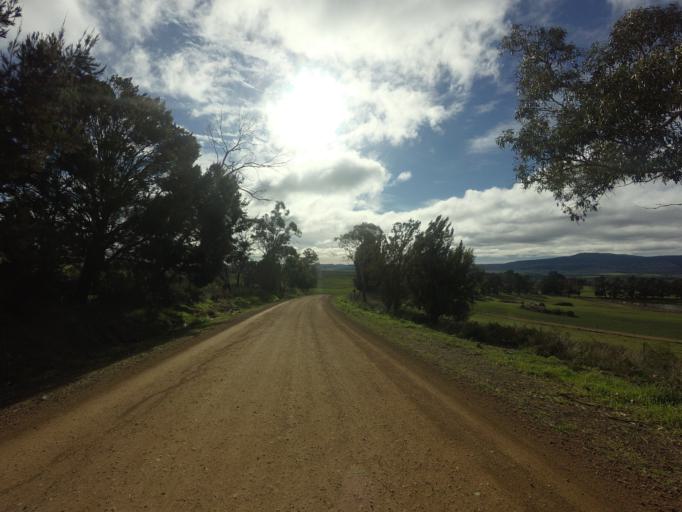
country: AU
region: Tasmania
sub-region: Derwent Valley
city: New Norfolk
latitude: -42.7198
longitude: 146.8739
